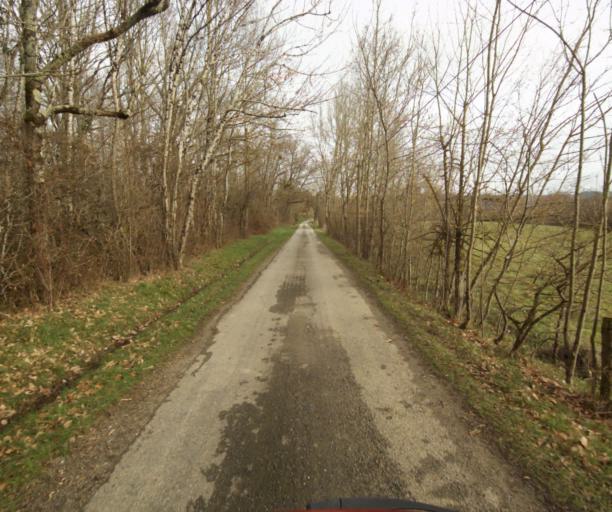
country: FR
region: Midi-Pyrenees
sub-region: Departement de la Haute-Garonne
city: Gaillac-Toulza
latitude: 43.1631
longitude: 1.4860
